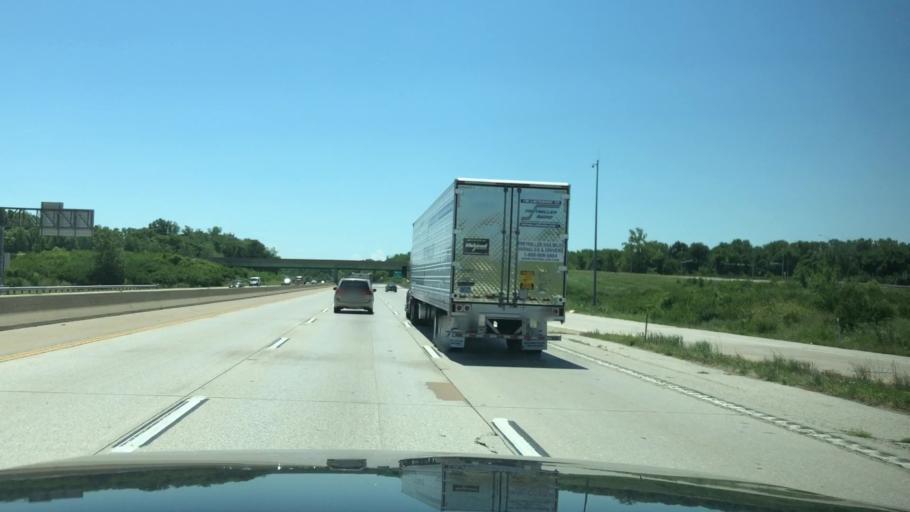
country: US
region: Missouri
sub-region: Saint Louis County
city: Bridgeton
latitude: 38.7829
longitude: -90.4180
